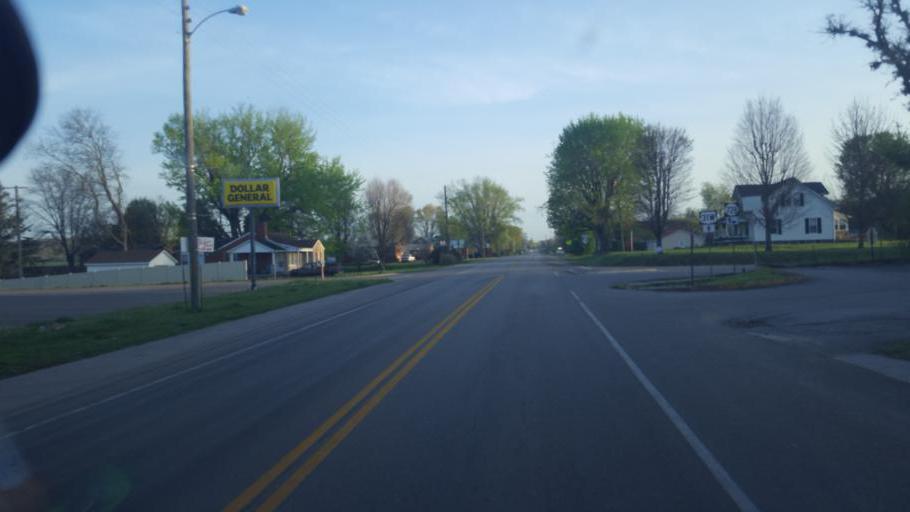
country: US
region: Kentucky
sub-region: Hart County
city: Munfordville
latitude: 37.3781
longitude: -85.9029
